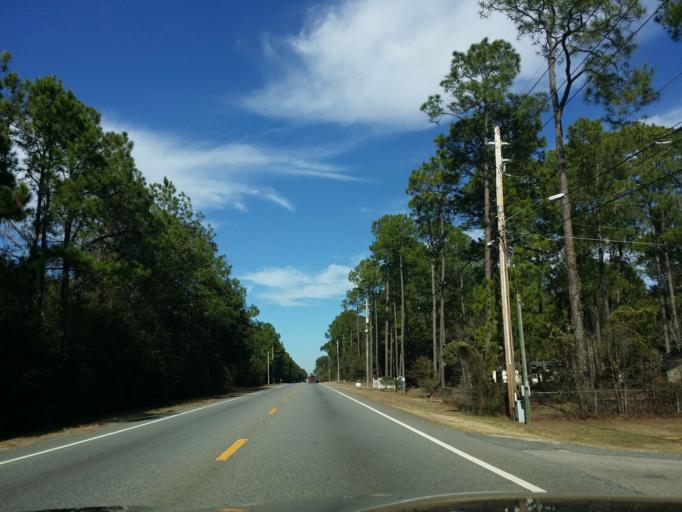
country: US
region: Florida
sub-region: Leon County
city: Woodville
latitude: 30.3563
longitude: -84.2617
